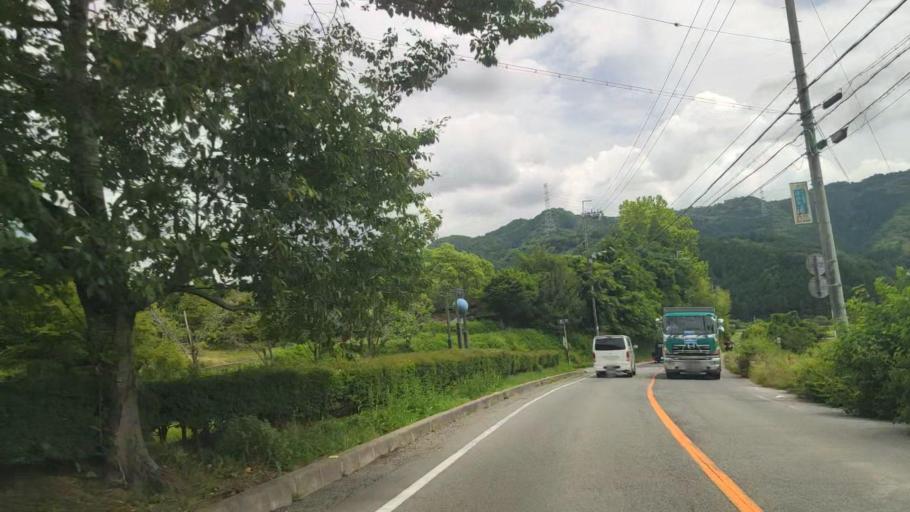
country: JP
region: Hyogo
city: Yamazakicho-nakabirose
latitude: 34.9861
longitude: 134.4133
